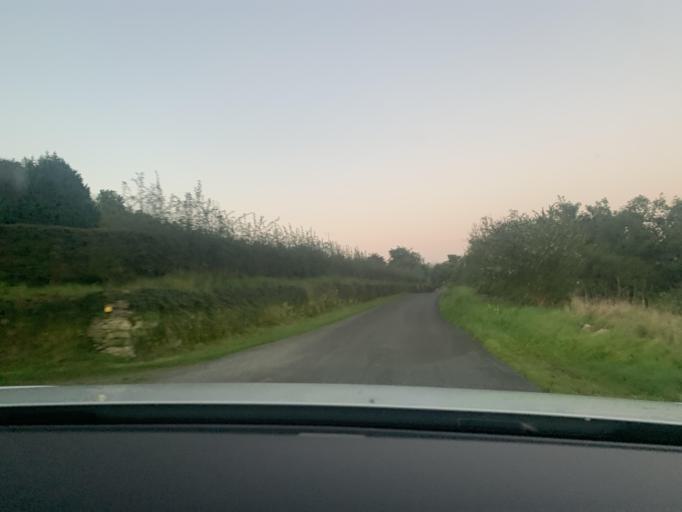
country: IE
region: Connaught
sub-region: County Leitrim
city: Manorhamilton
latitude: 54.2631
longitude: -8.2950
